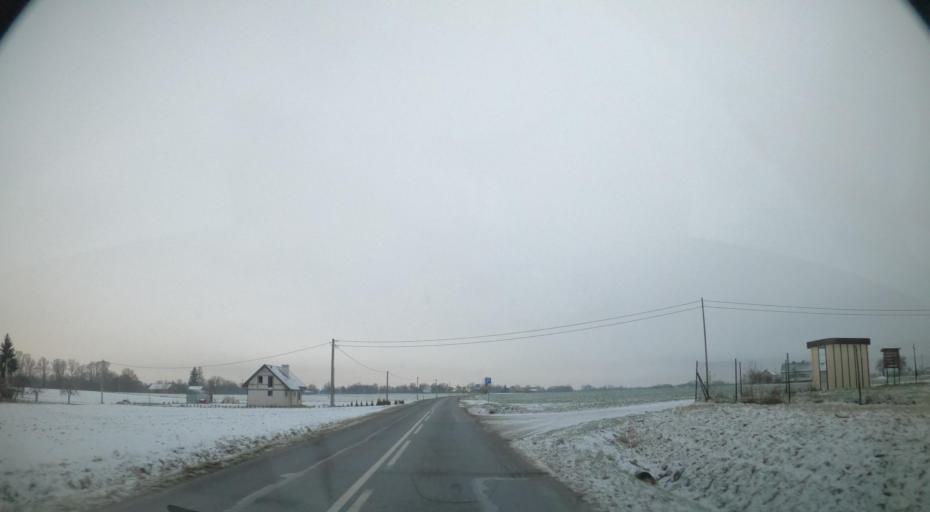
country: PL
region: Kujawsko-Pomorskie
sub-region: Powiat lipnowski
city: Dobrzyn nad Wisla
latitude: 52.6506
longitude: 19.3922
